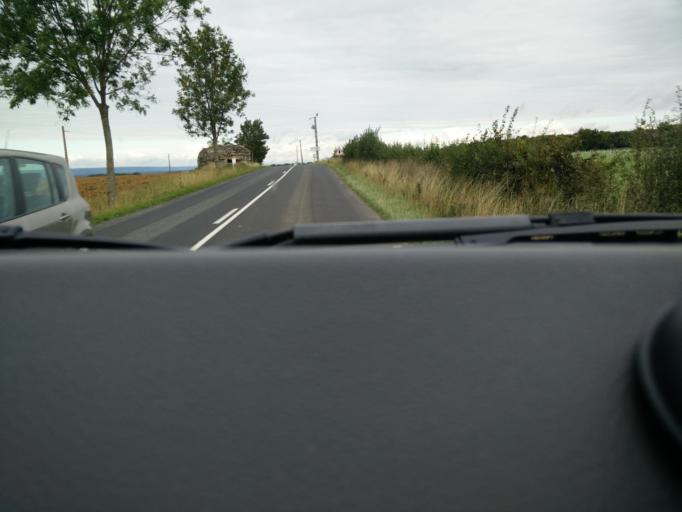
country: FR
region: Lorraine
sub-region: Departement de Meurthe-et-Moselle
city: Montauville
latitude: 48.9289
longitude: 5.9023
